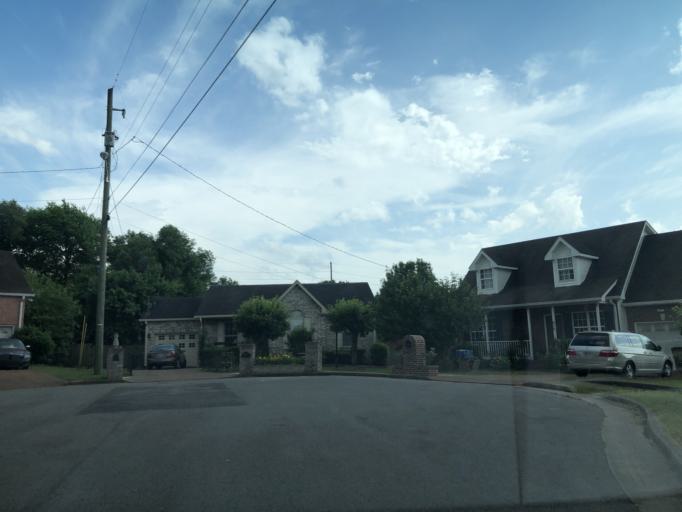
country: US
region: Tennessee
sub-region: Davidson County
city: Goodlettsville
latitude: 36.2759
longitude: -86.7060
